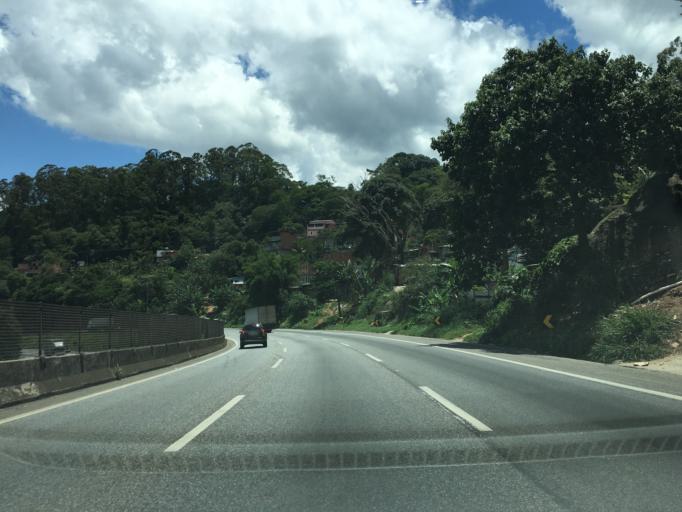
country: BR
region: Sao Paulo
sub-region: Guarulhos
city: Guarulhos
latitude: -23.3977
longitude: -46.5757
